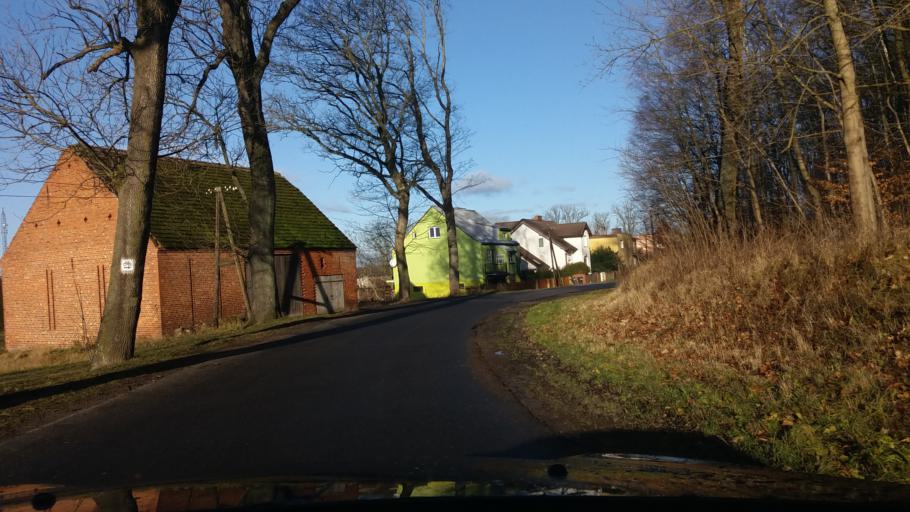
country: PL
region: West Pomeranian Voivodeship
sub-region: Powiat choszczenski
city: Drawno
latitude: 53.2117
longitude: 15.7711
